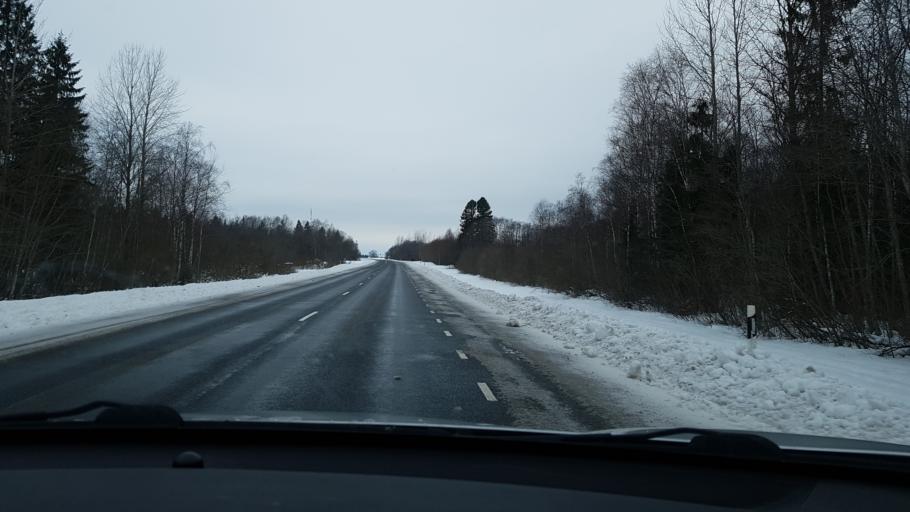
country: EE
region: Jaervamaa
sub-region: Jaerva-Jaani vald
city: Jarva-Jaani
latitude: 58.8967
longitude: 25.7776
